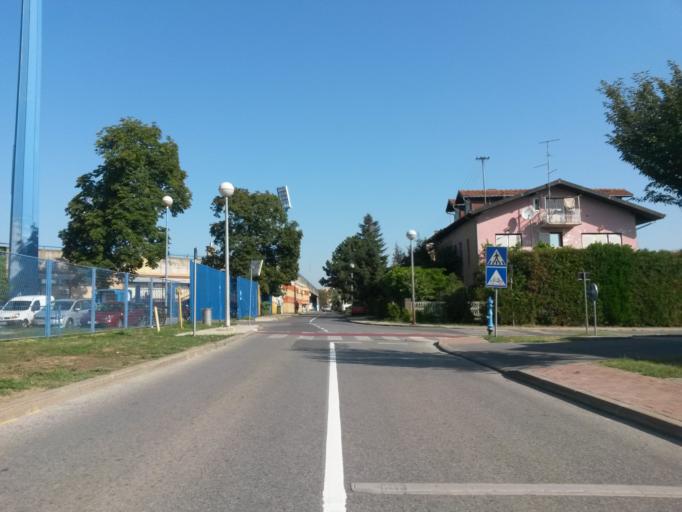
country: HR
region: Osjecko-Baranjska
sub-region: Grad Osijek
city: Osijek
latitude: 45.5437
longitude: 18.6968
